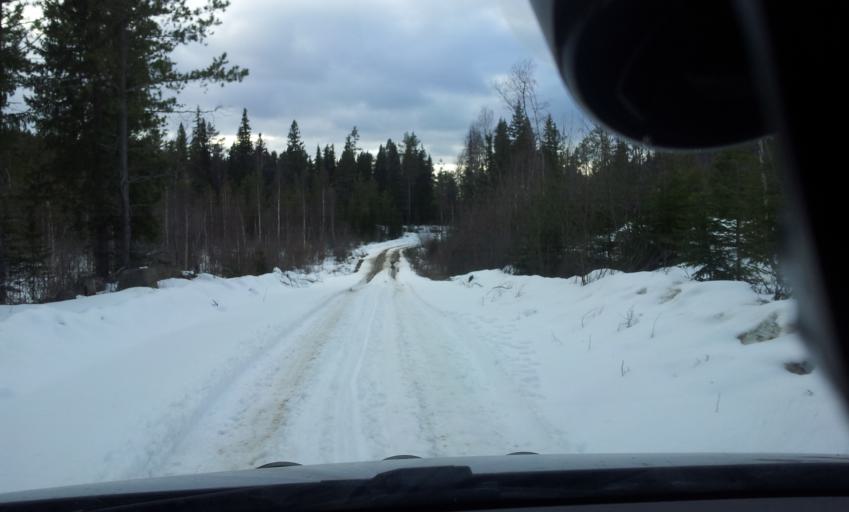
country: SE
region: Vaesternorrland
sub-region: Ange Kommun
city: Ange
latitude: 62.1935
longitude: 15.7487
